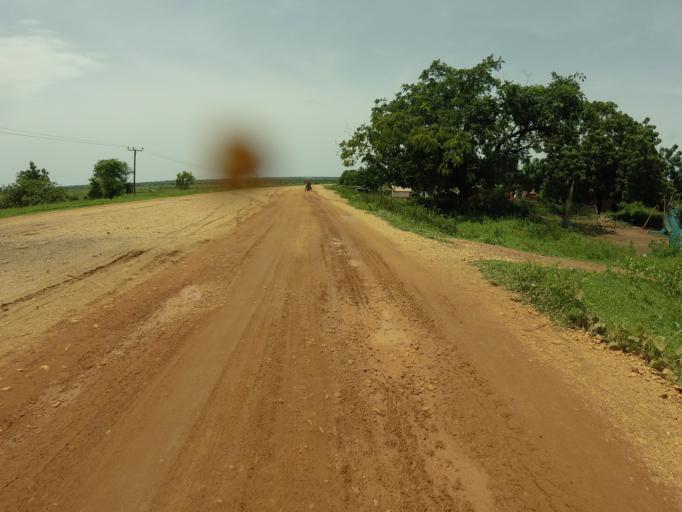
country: GH
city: Kpandae
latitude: 8.7048
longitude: 0.1633
